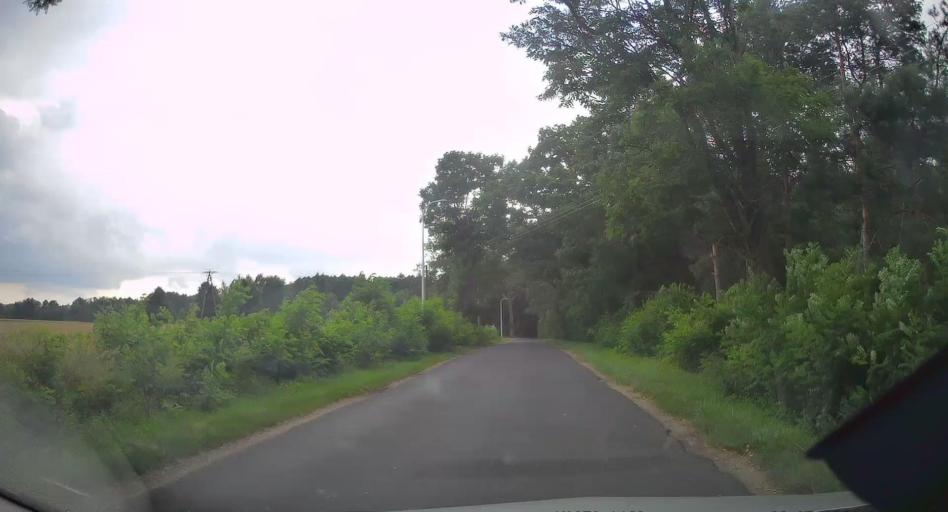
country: PL
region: Lodz Voivodeship
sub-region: Powiat rawski
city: Rawa Mazowiecka
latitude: 51.7389
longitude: 20.1925
